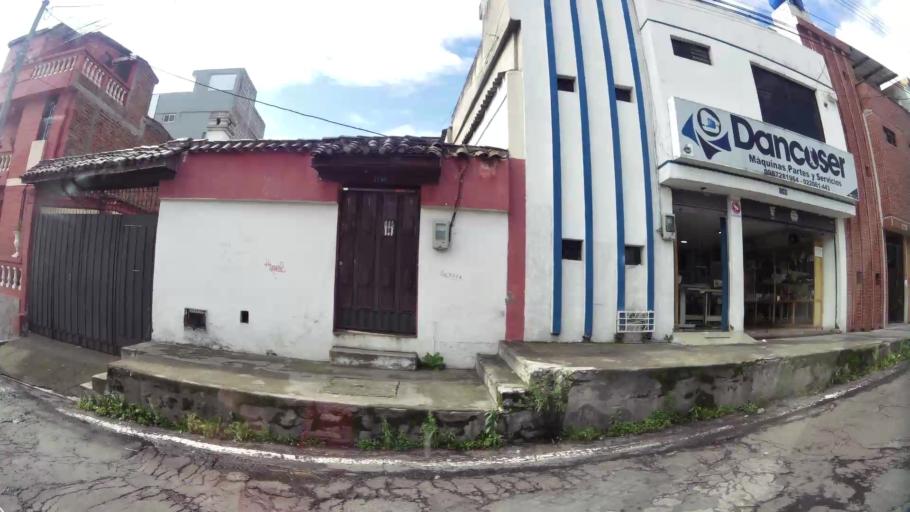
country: EC
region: Pichincha
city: Sangolqui
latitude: -0.3310
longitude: -78.4498
